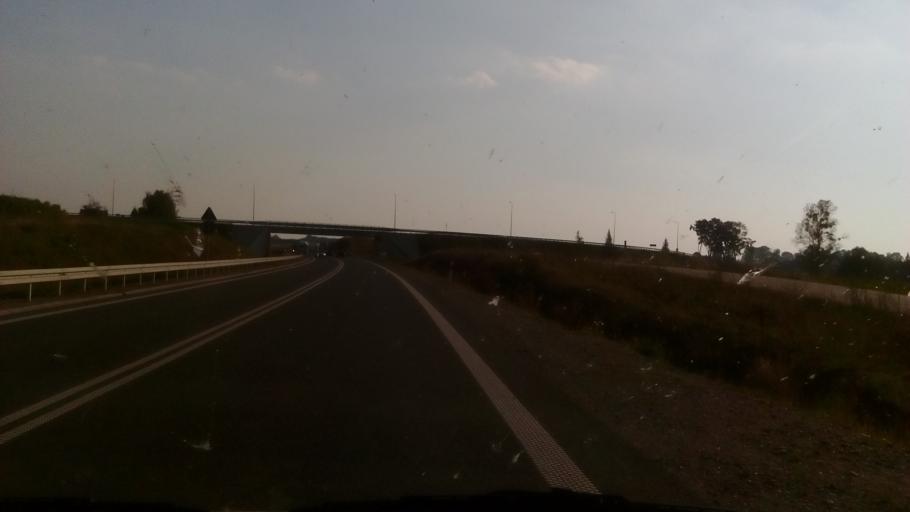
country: PL
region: Podlasie
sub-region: Powiat grajewski
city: Rajgrod
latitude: 53.7758
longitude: 22.8356
